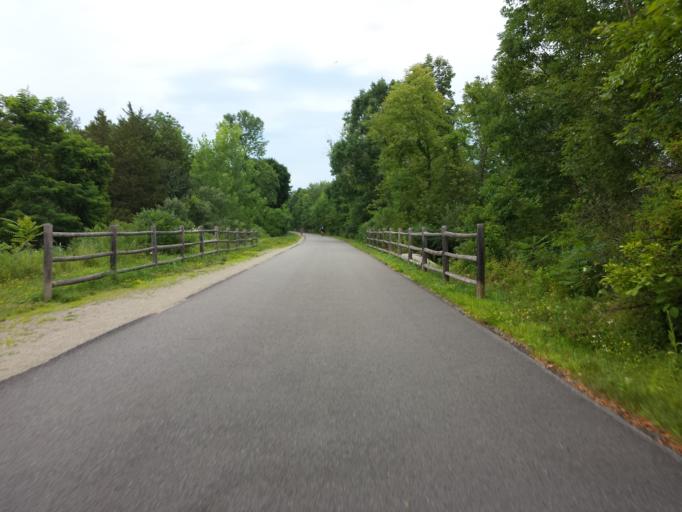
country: US
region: New York
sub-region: Dutchess County
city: Red Oaks Mill
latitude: 41.6670
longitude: -73.8551
